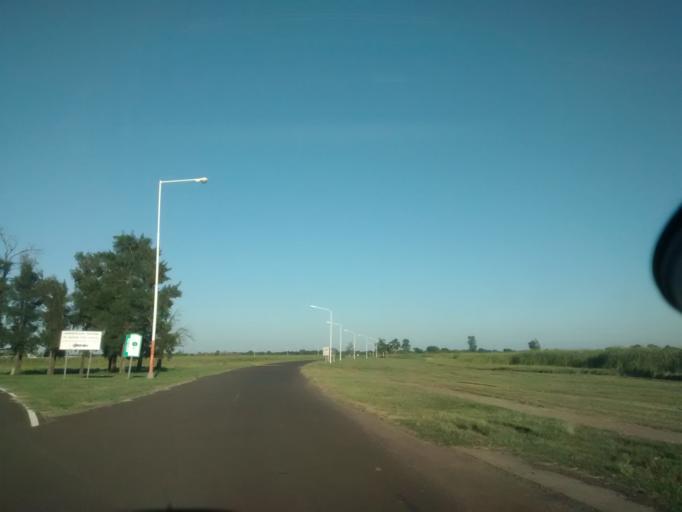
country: AR
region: Chaco
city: Fontana
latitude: -27.4429
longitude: -59.0420
